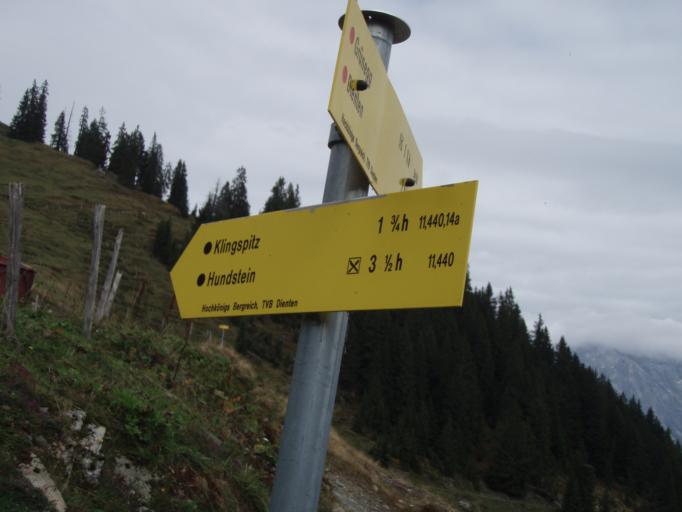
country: AT
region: Salzburg
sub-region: Politischer Bezirk Zell am See
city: Dienten am Hochkonig
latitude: 47.3593
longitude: 12.9694
